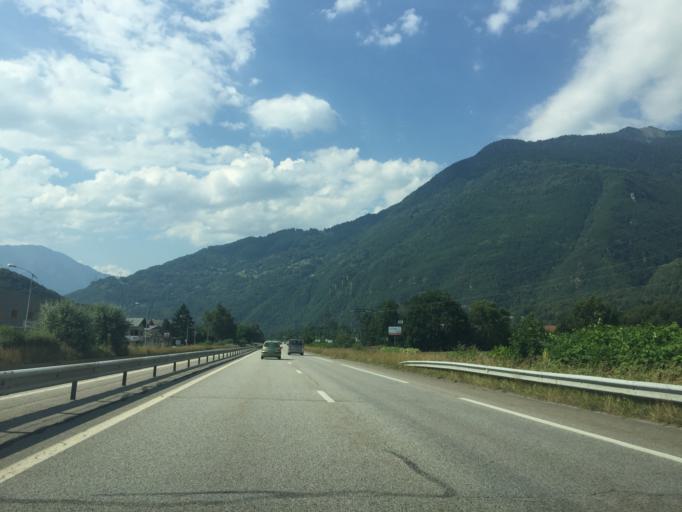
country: FR
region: Rhone-Alpes
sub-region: Departement de la Savoie
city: La Bathie
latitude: 45.6418
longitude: 6.4398
